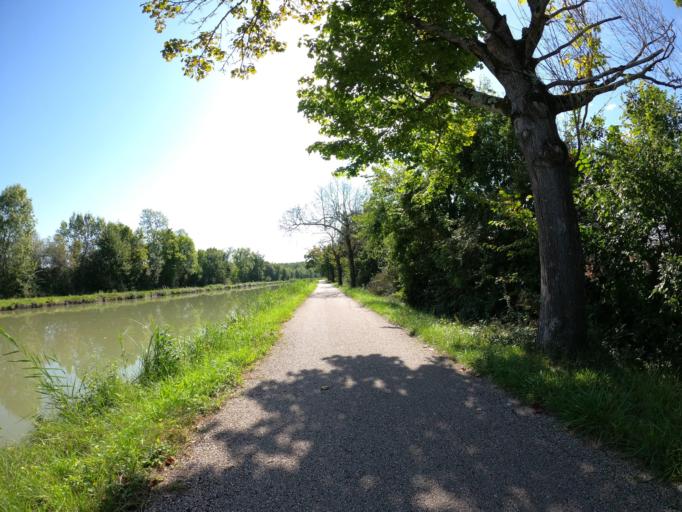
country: FR
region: Midi-Pyrenees
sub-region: Departement du Tarn-et-Garonne
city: Montech
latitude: 43.9480
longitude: 1.2520
